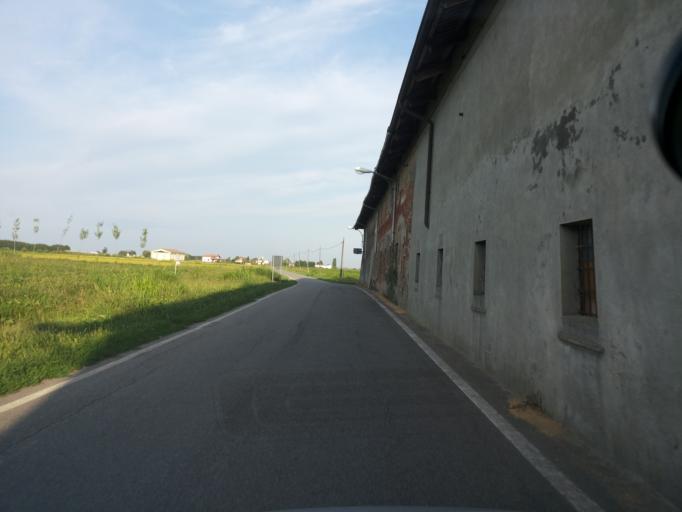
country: IT
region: Piedmont
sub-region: Provincia di Vercelli
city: Crova
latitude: 45.3286
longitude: 8.2163
